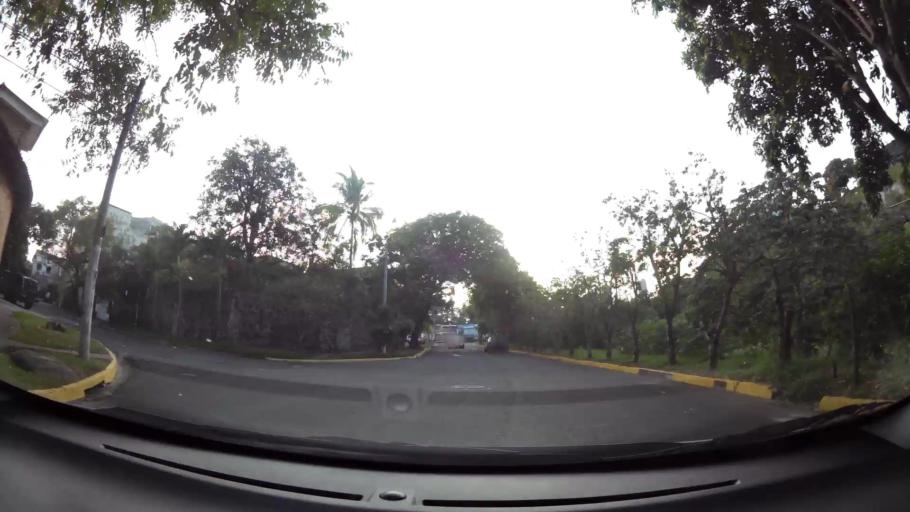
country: SV
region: La Libertad
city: Antiguo Cuscatlan
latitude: 13.7023
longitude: -89.2484
